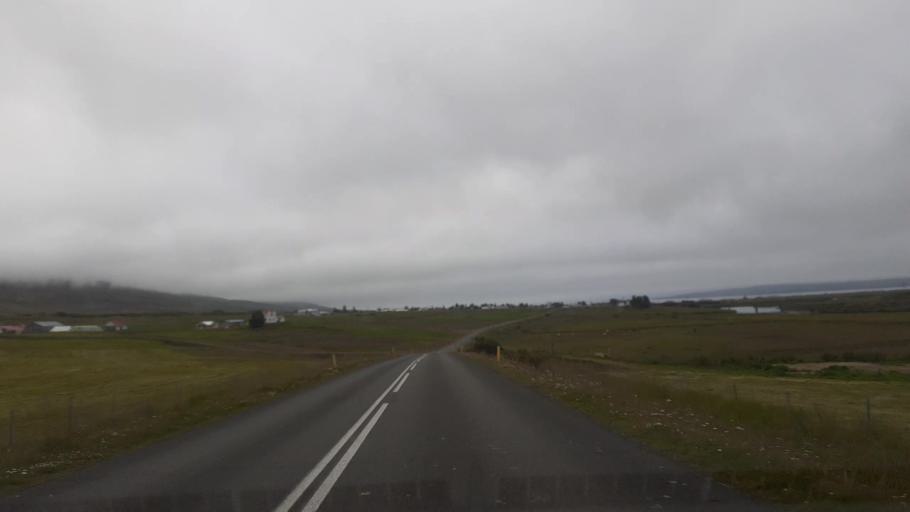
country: IS
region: Northeast
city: Dalvik
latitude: 65.9544
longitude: -18.5511
